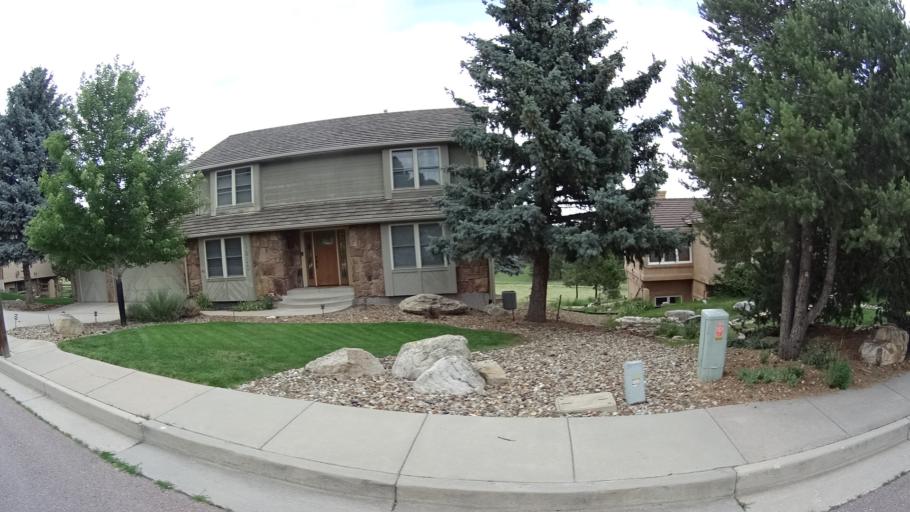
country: US
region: Colorado
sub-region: El Paso County
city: Colorado Springs
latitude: 38.9106
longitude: -104.8487
